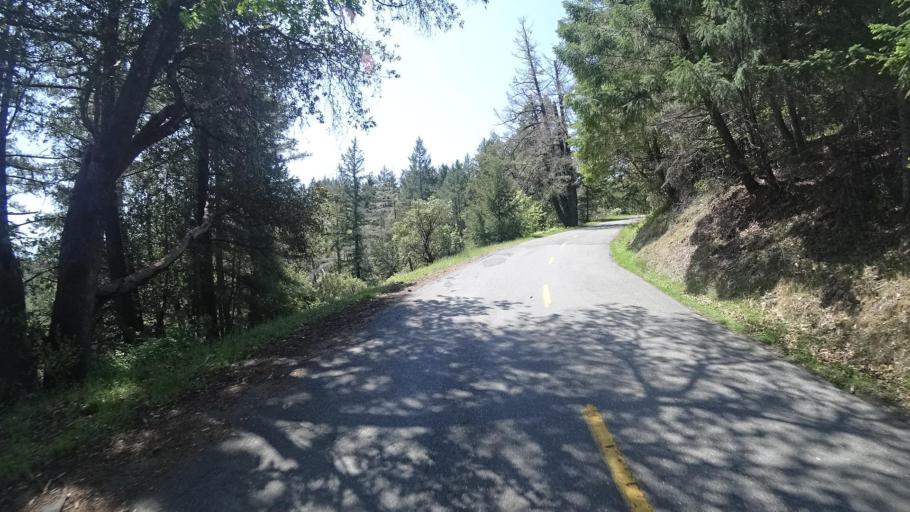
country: US
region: California
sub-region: Humboldt County
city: Redway
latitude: 40.1599
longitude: -123.6154
